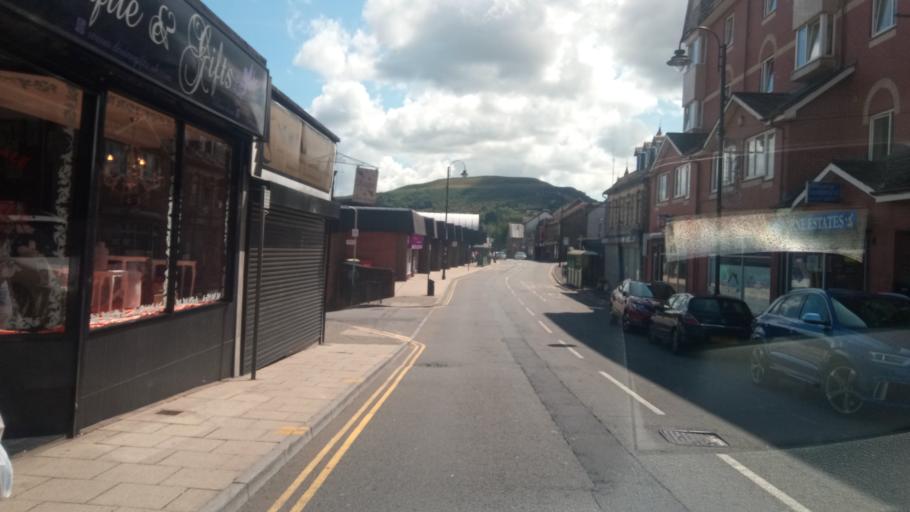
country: GB
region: Wales
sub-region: Rhondda Cynon Taf
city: Tonypandy
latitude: 51.6210
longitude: -3.4531
